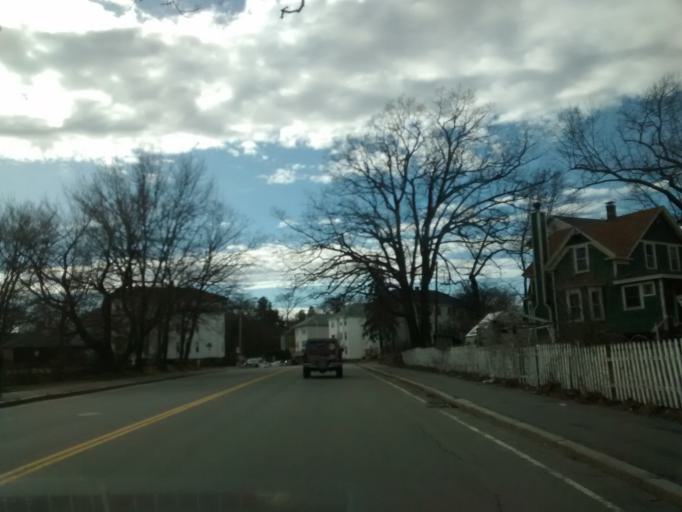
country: US
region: Massachusetts
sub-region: Worcester County
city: Sunderland
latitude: 42.2505
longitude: -71.7708
